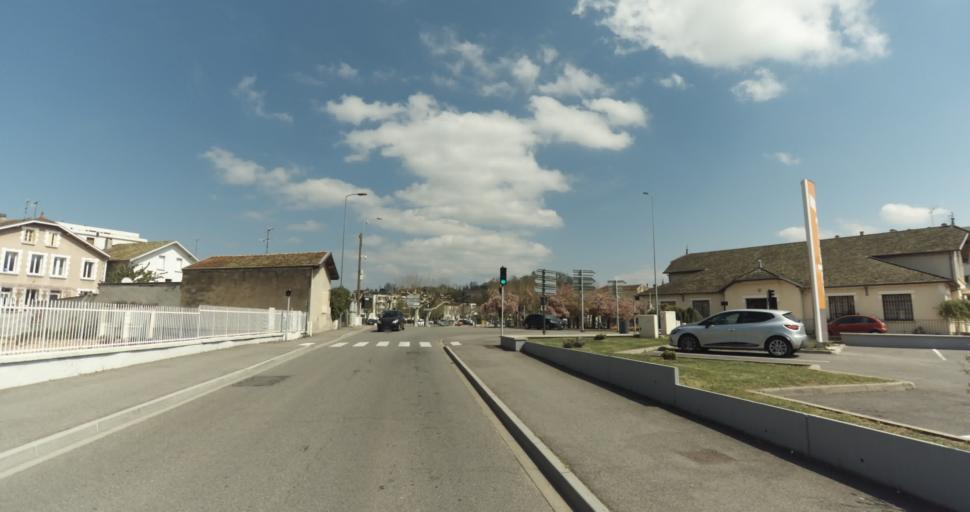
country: FR
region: Rhone-Alpes
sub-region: Departement de l'Isere
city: Saint-Marcellin
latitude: 45.1537
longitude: 5.3172
